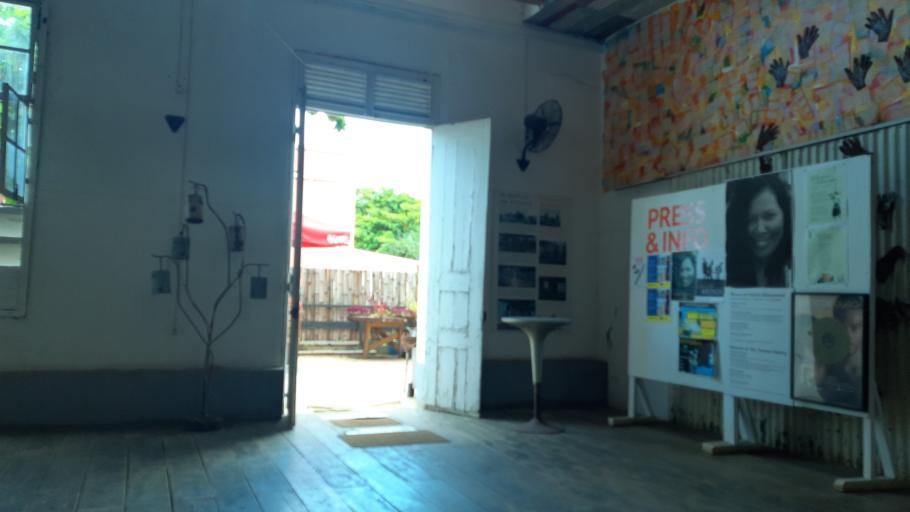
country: ST
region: Sao Tome Island
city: Sao Tome
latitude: 0.3439
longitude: 6.7375
